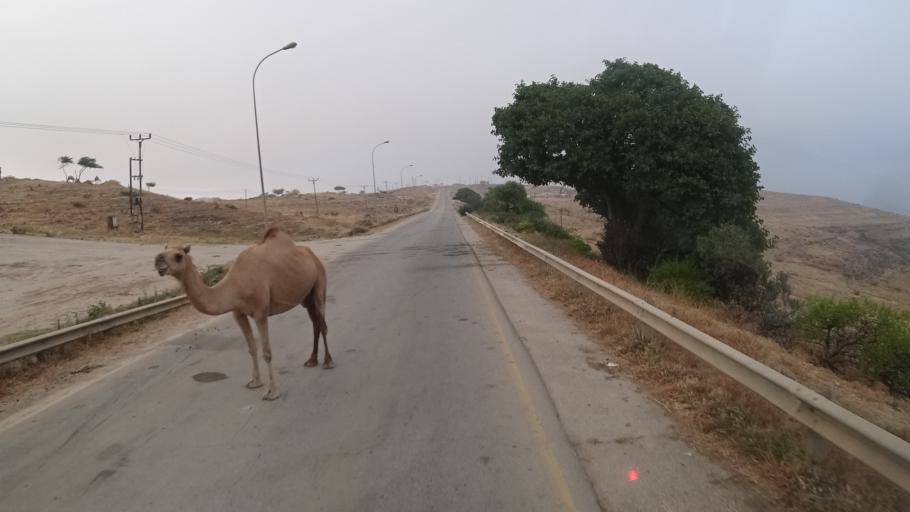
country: OM
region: Zufar
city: Salalah
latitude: 17.1248
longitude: 53.9759
